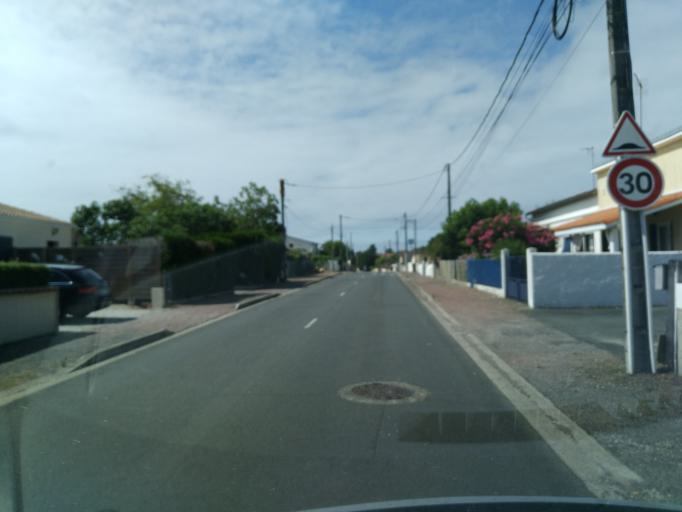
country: FR
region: Poitou-Charentes
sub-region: Departement de la Charente-Maritime
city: Vaux-sur-Mer
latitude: 45.6595
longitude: -1.0750
